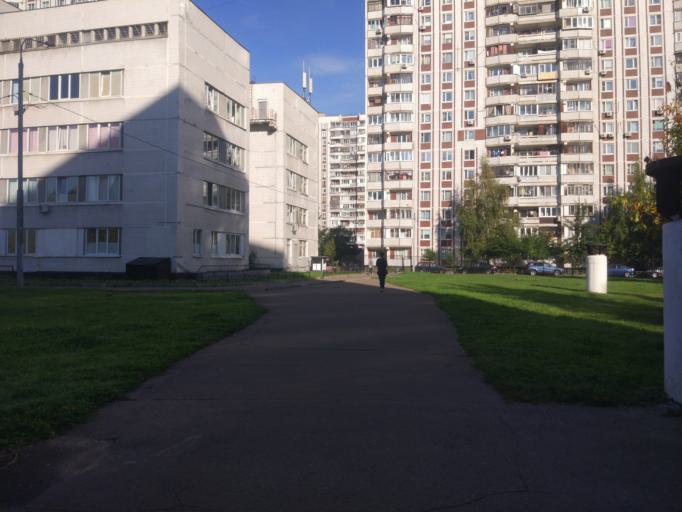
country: RU
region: Moskovskaya
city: Reutov
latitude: 55.7424
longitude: 37.8760
